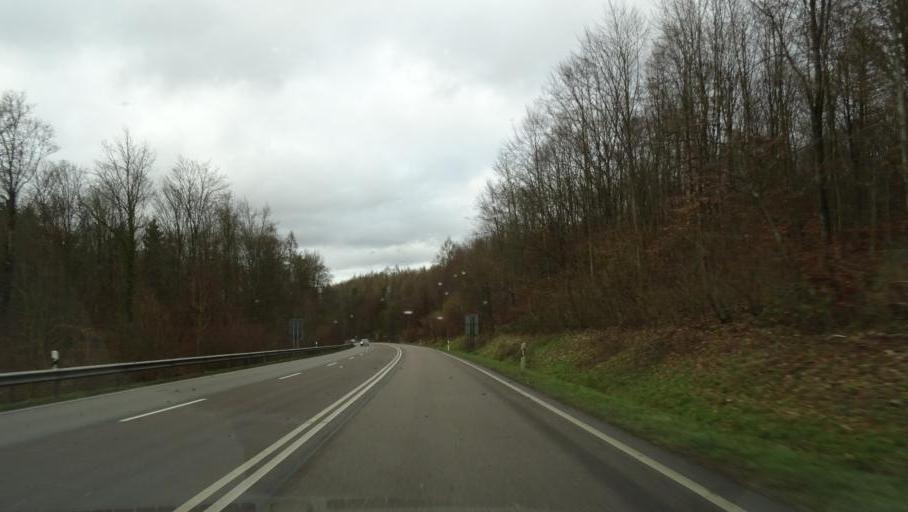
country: DE
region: Baden-Wuerttemberg
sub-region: Karlsruhe Region
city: Waibstadt
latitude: 49.2760
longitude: 8.9074
